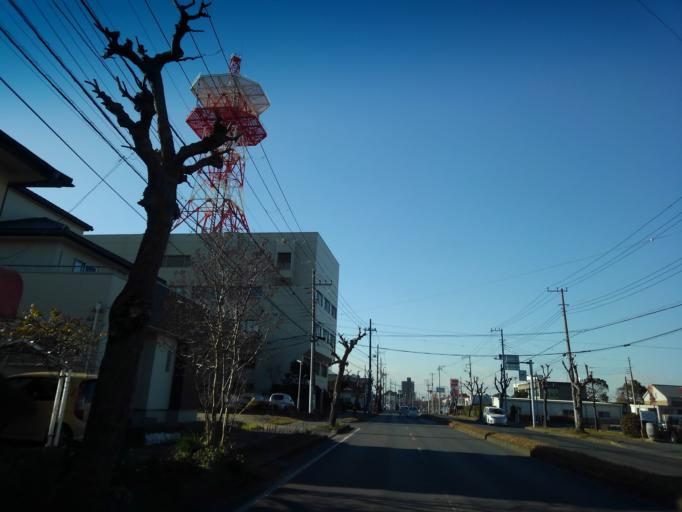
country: JP
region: Chiba
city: Kimitsu
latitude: 35.3260
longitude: 139.9079
